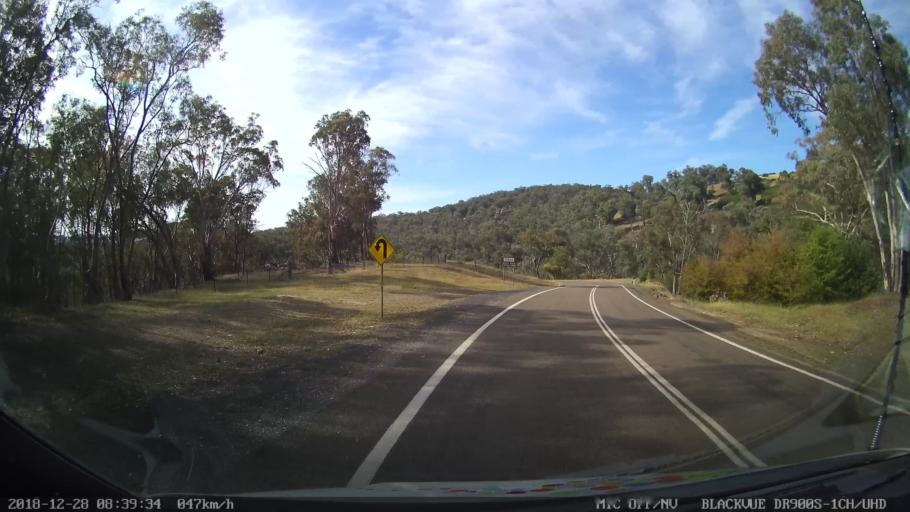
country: AU
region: New South Wales
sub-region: Upper Lachlan Shire
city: Crookwell
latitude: -34.0131
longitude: 149.3185
